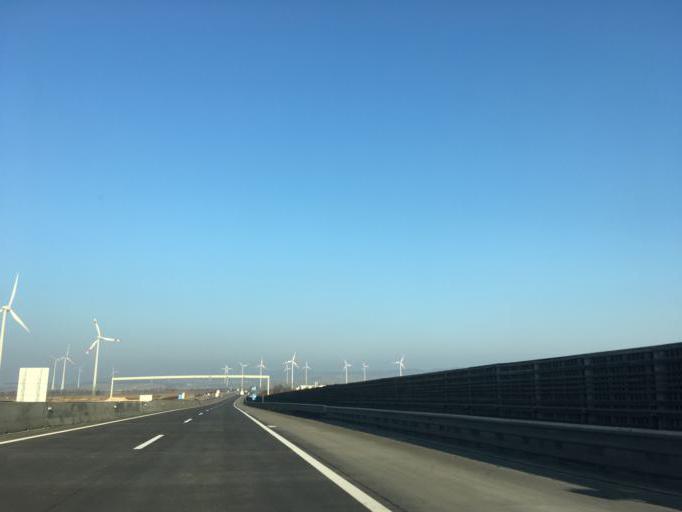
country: AT
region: Burgenland
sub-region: Politischer Bezirk Neusiedl am See
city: Kittsee
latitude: 48.0749
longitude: 17.0601
